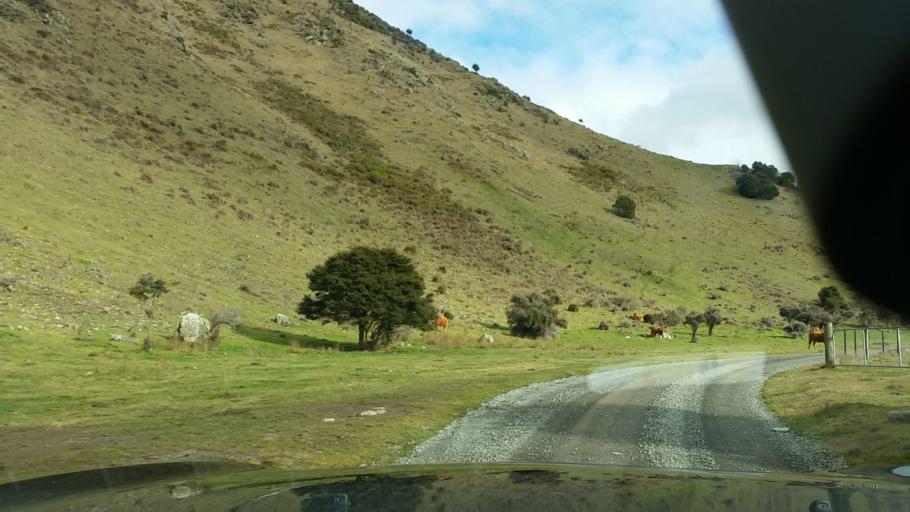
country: NZ
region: Tasman
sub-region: Tasman District
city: Richmond
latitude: -41.7310
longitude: 173.4656
